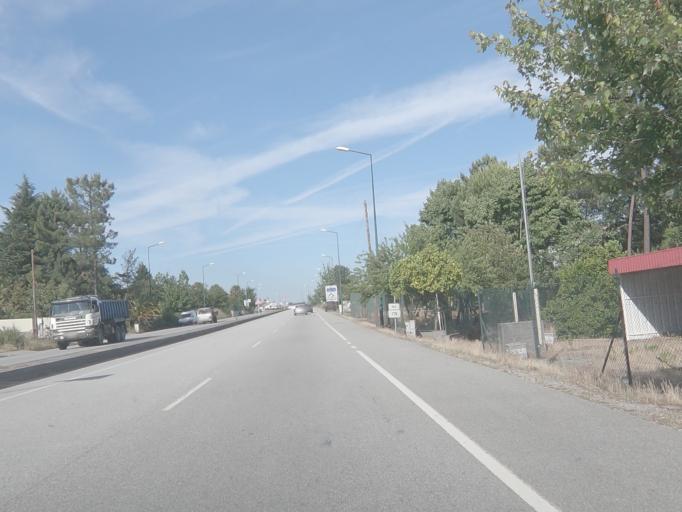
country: PT
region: Viseu
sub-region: Viseu
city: Viseu
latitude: 40.6206
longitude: -7.9492
